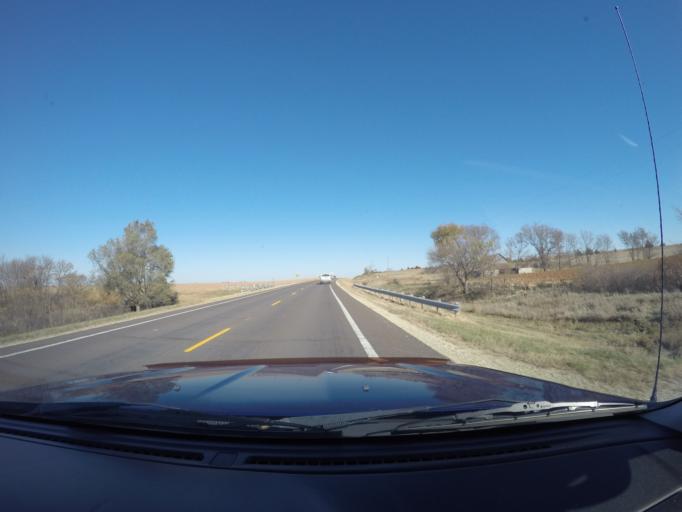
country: US
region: Kansas
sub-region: Marshall County
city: Blue Rapids
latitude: 39.5223
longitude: -96.7554
